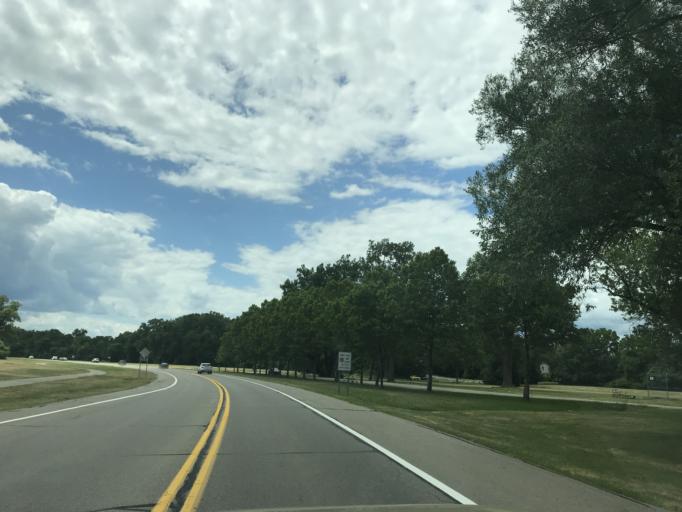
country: US
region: Michigan
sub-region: Wayne County
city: Dearborn Heights
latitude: 42.3475
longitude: -83.2768
